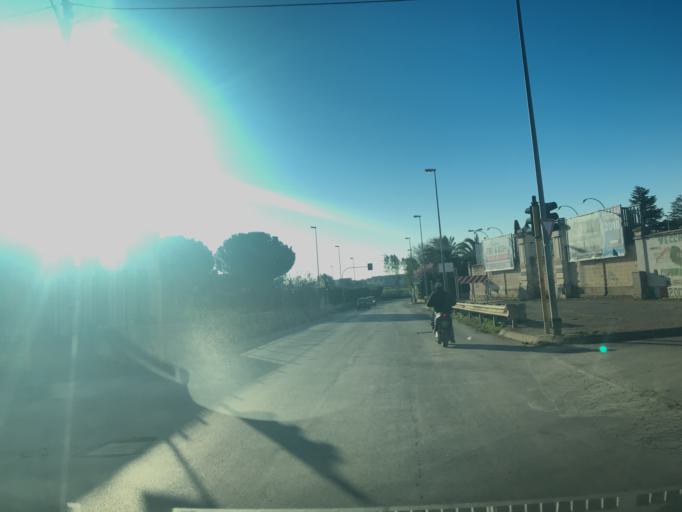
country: IT
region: Apulia
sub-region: Provincia di Bari
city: Corato
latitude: 41.1426
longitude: 16.4141
